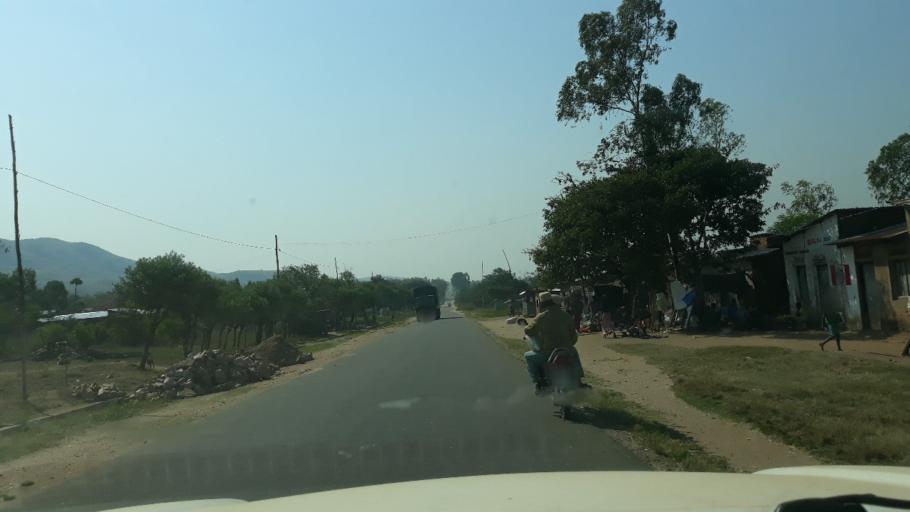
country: CD
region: South Kivu
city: Uvira
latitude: -3.2283
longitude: 29.1660
